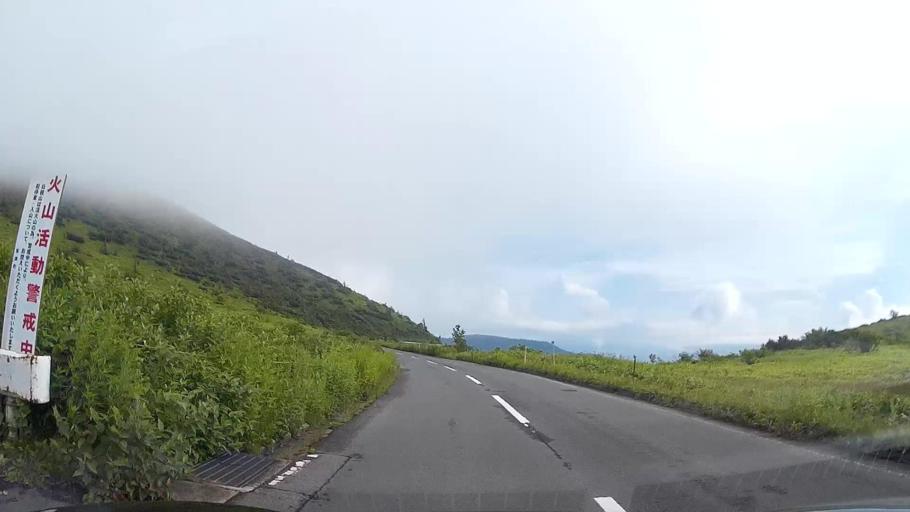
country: JP
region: Nagano
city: Nakano
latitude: 36.6488
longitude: 138.5254
